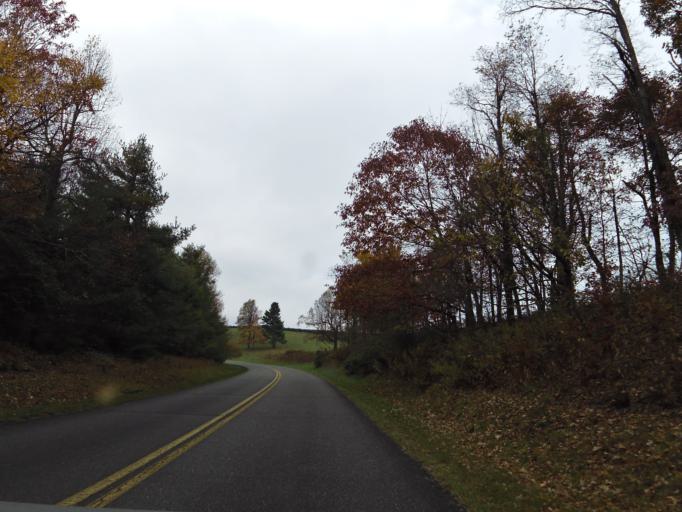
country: US
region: North Carolina
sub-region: Ashe County
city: West Jefferson
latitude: 36.2785
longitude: -81.3810
